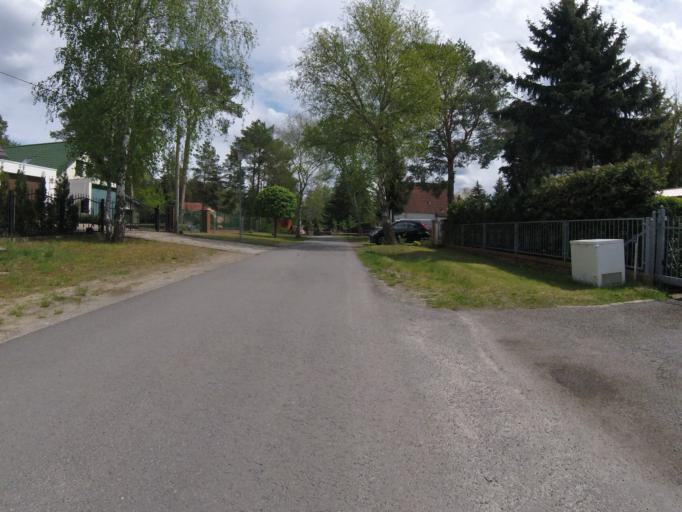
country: DE
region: Brandenburg
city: Schwerin
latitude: 52.1586
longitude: 13.6306
